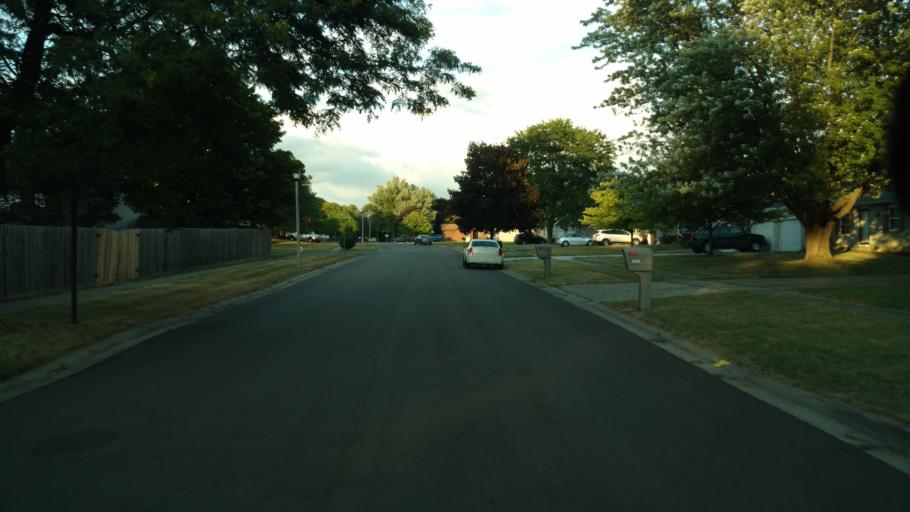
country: US
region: Michigan
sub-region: Eaton County
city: Waverly
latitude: 42.7216
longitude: -84.6128
